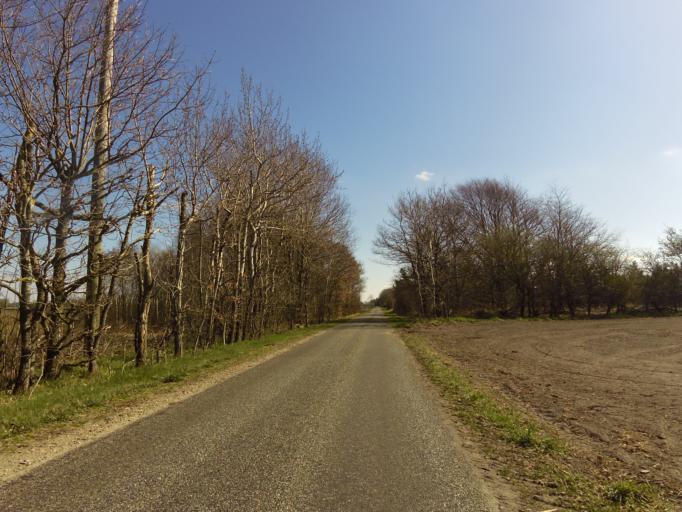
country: DK
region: South Denmark
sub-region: Esbjerg Kommune
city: Ribe
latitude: 55.3427
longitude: 8.8566
